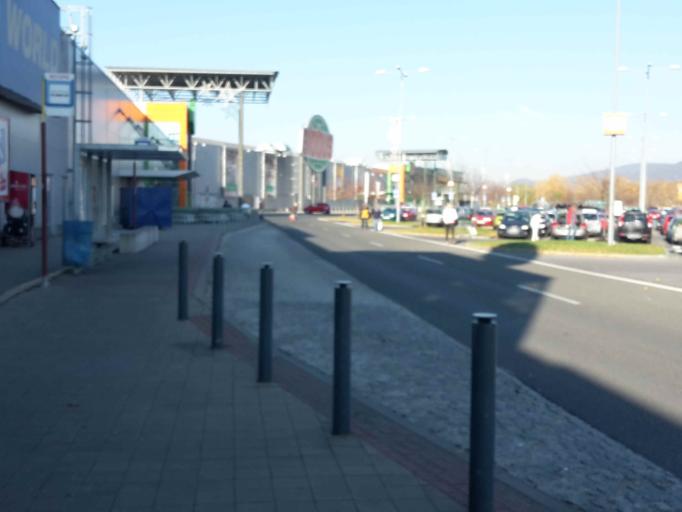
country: CZ
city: Straz nad Nisou
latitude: 50.7759
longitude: 15.0292
